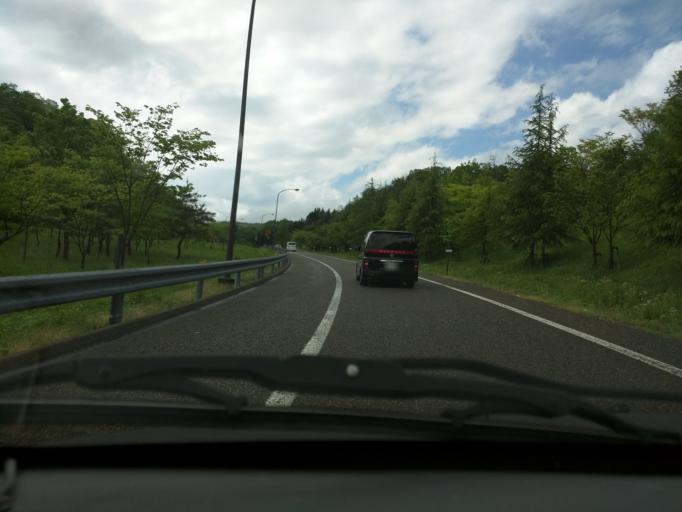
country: JP
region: Niigata
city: Joetsu
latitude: 37.1392
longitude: 138.2153
